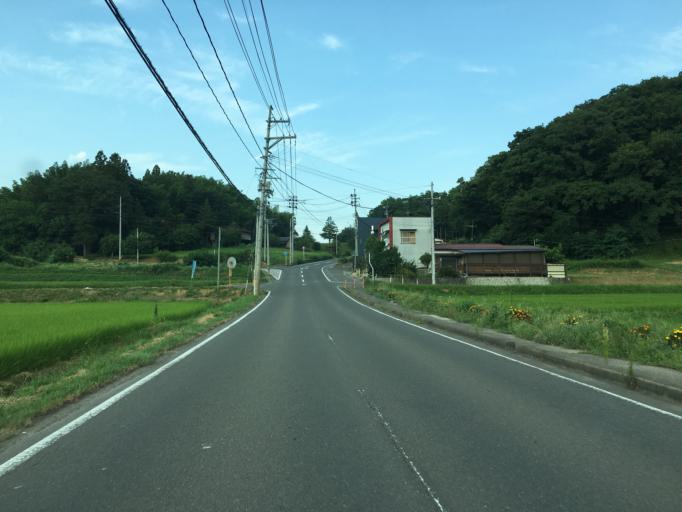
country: JP
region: Fukushima
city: Nihommatsu
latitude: 37.5804
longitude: 140.4354
